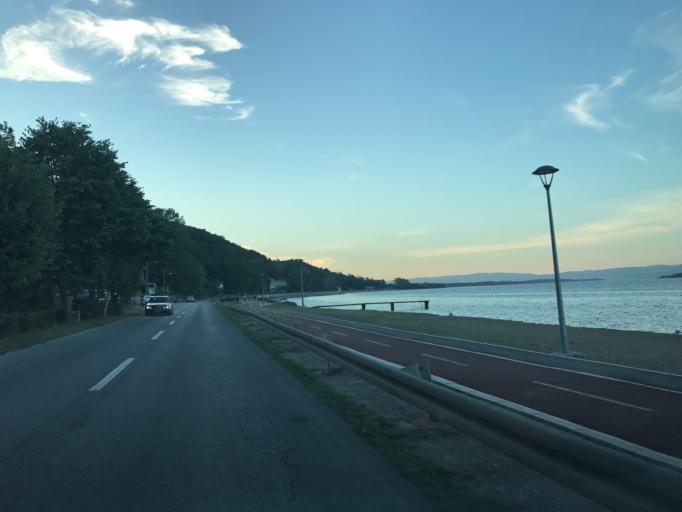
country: RS
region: Central Serbia
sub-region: Branicevski Okrug
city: Golubac
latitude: 44.6560
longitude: 21.6202
